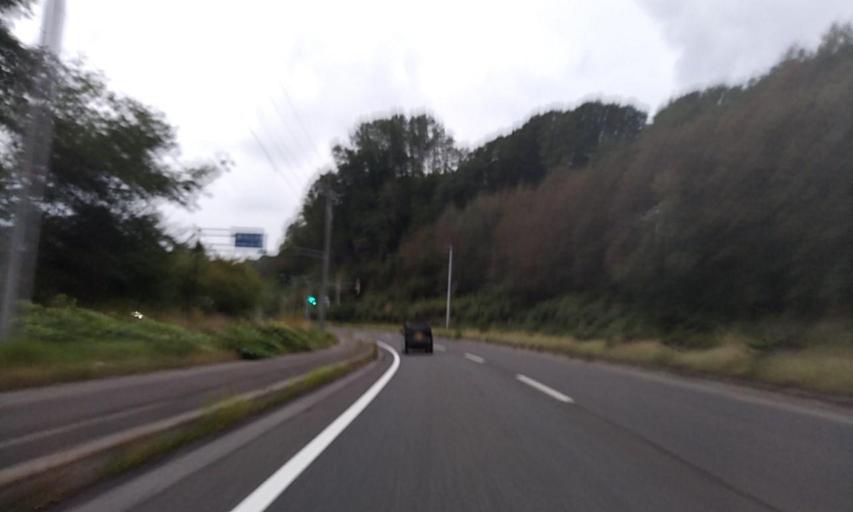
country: JP
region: Hokkaido
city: Abashiri
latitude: 44.0154
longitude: 144.2812
